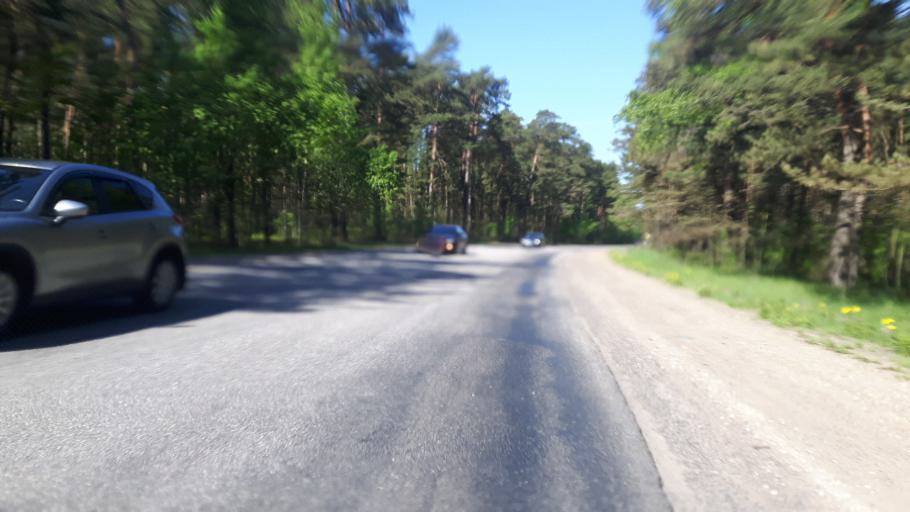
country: RU
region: Leningrad
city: Lebyazh'ye
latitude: 59.9581
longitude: 29.4441
